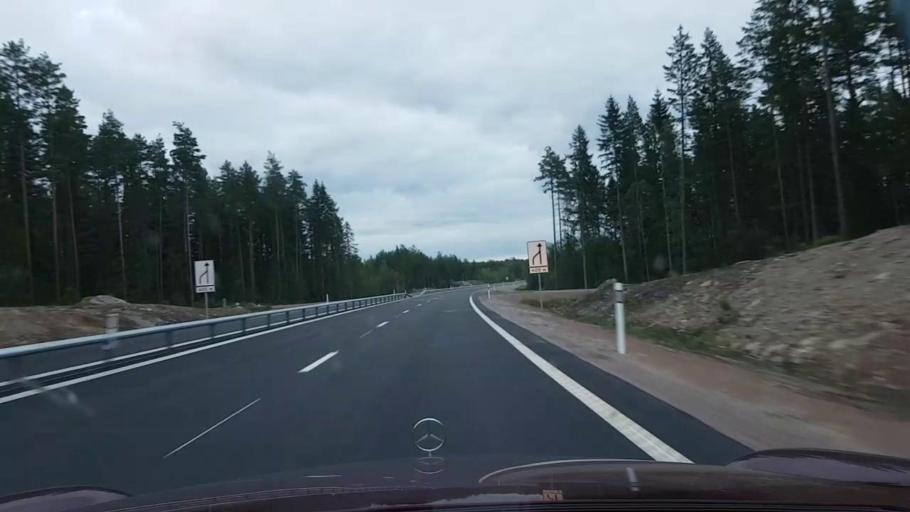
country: SE
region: Vaestmanland
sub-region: Surahammars Kommun
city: Surahammar
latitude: 59.6831
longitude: 16.2399
